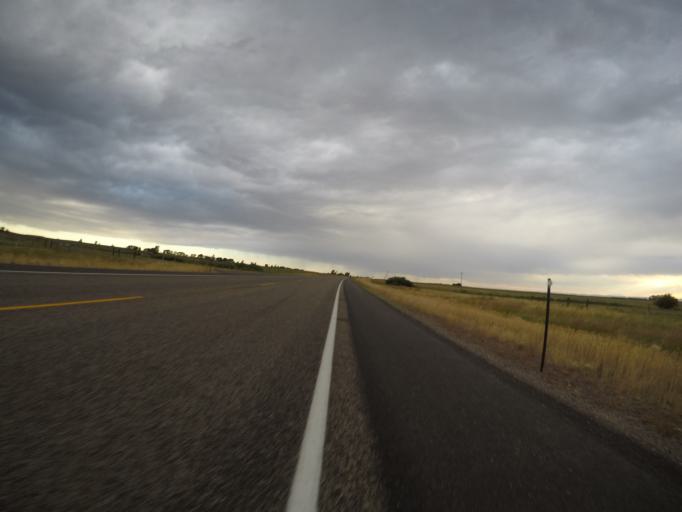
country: US
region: Wyoming
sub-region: Albany County
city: Laramie
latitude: 41.7786
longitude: -105.9825
